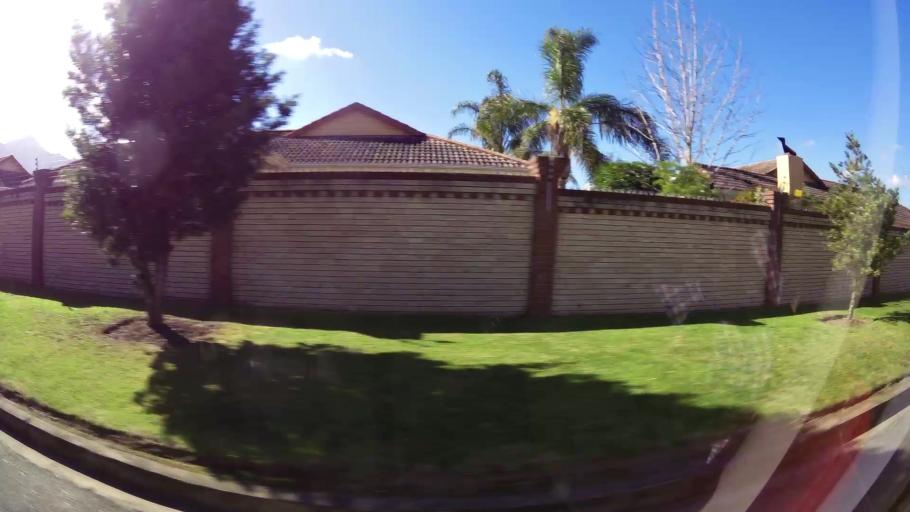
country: ZA
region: Western Cape
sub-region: Eden District Municipality
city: George
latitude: -33.9546
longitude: 22.4325
